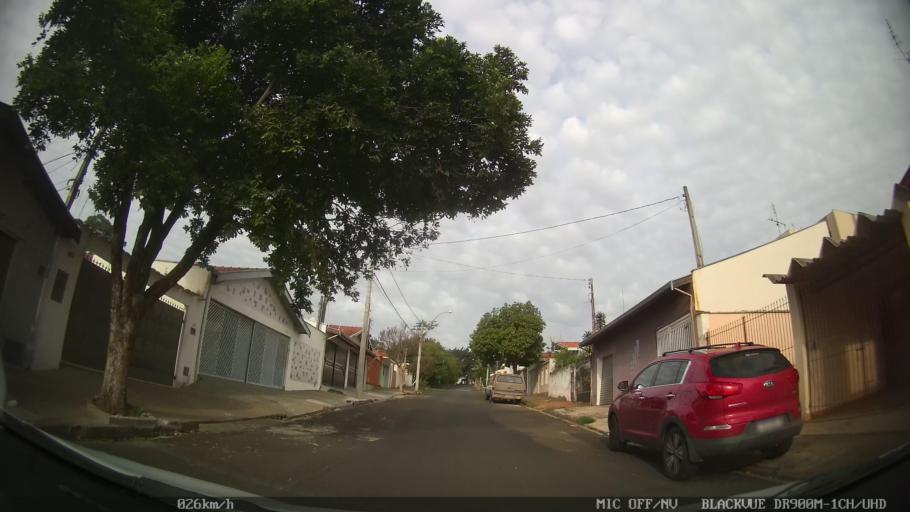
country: BR
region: Sao Paulo
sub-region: Piracicaba
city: Piracicaba
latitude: -22.7364
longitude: -47.6270
